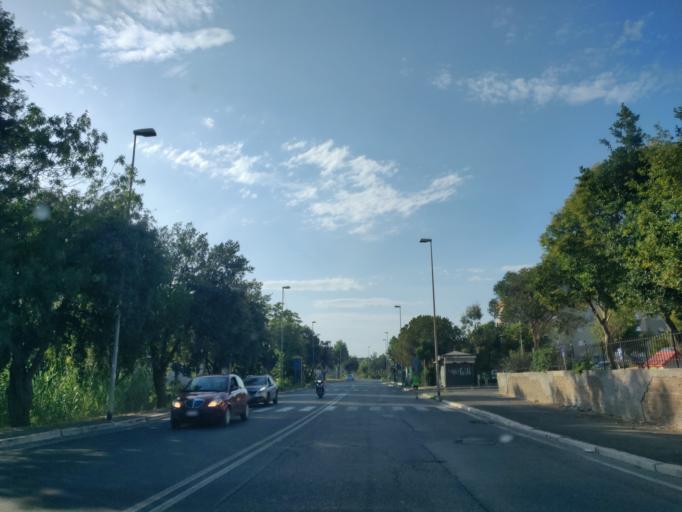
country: IT
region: Latium
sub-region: Citta metropolitana di Roma Capitale
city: Civitavecchia
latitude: 42.0778
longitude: 11.8149
